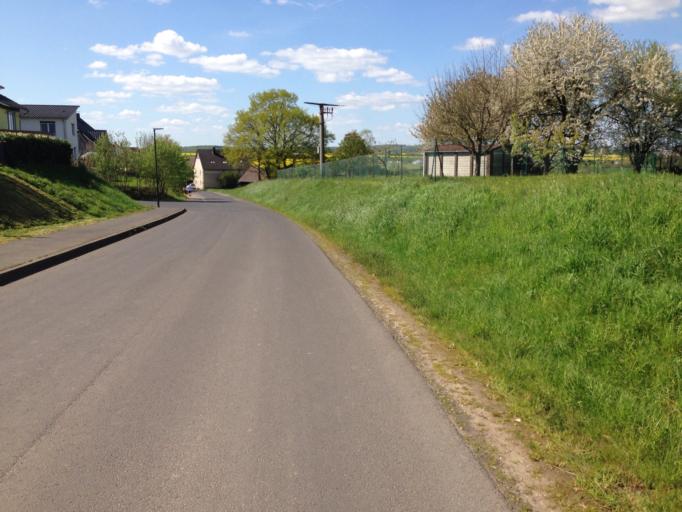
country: DE
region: Hesse
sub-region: Regierungsbezirk Giessen
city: Laubach
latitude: 50.5471
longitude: 8.9630
